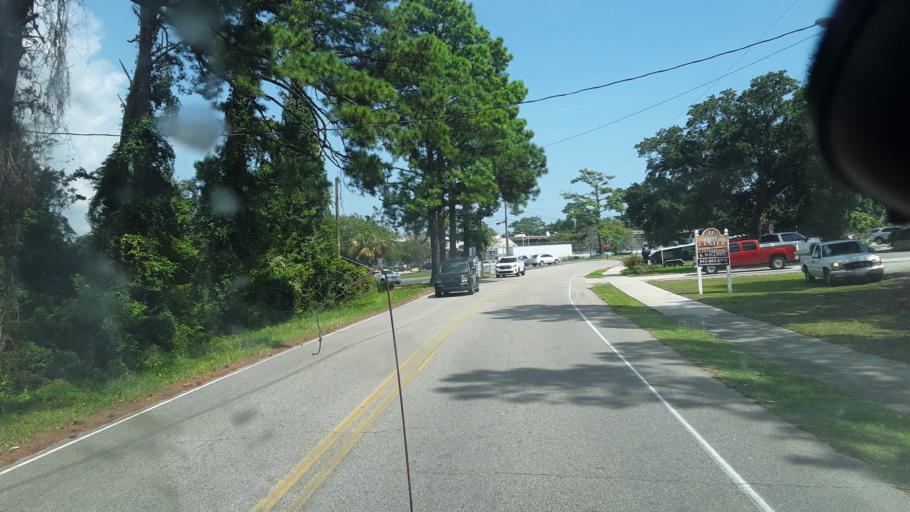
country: US
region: South Carolina
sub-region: Horry County
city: North Myrtle Beach
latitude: 33.8284
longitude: -78.6777
